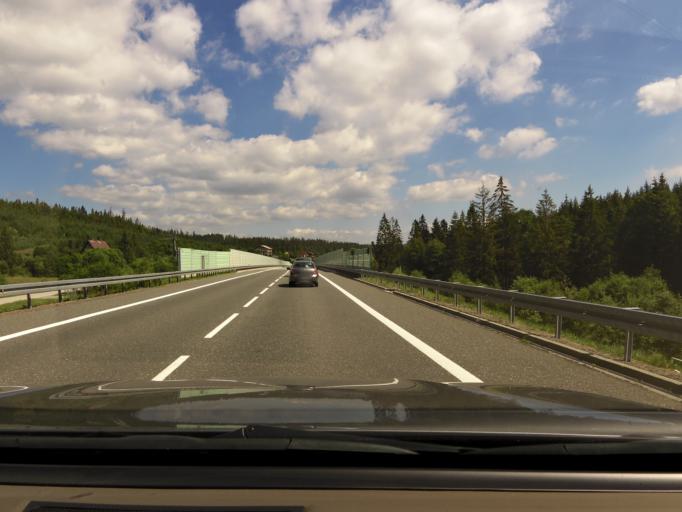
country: PL
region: Silesian Voivodeship
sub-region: Powiat zywiecki
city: Laliki
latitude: 49.5168
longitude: 18.9832
